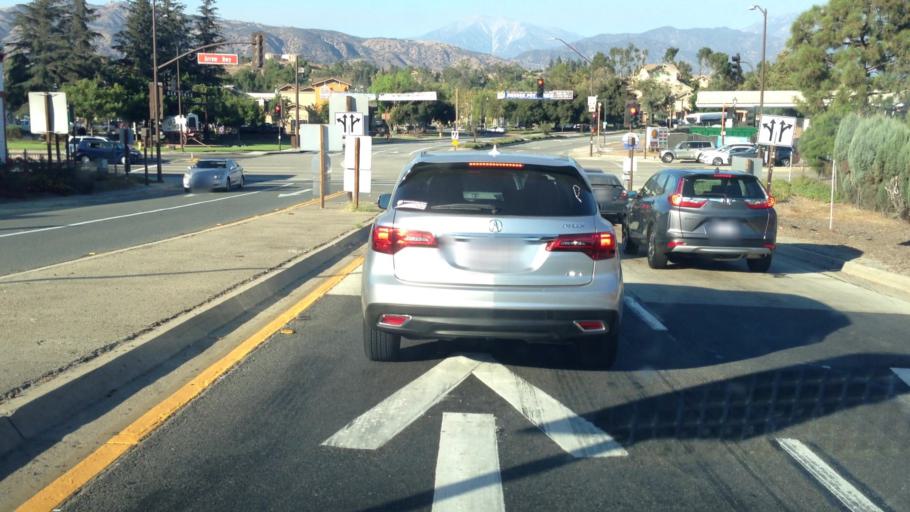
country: US
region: California
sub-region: Los Angeles County
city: San Dimas
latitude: 34.1056
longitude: -117.8200
